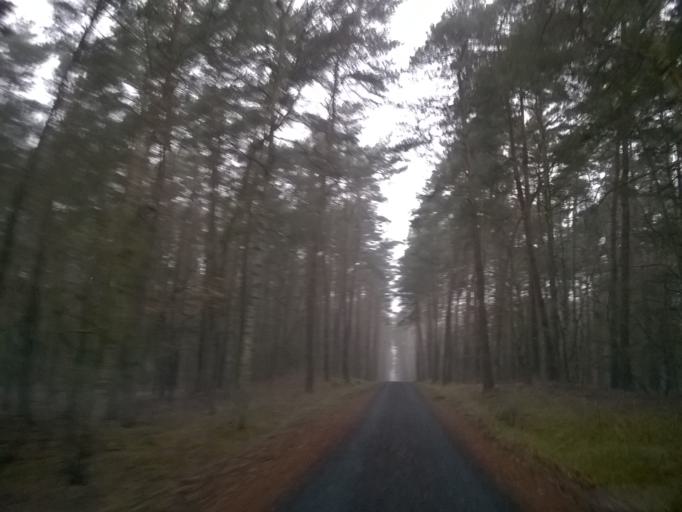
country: PL
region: Kujawsko-Pomorskie
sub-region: Powiat nakielski
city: Kcynia
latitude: 53.0506
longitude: 17.4703
